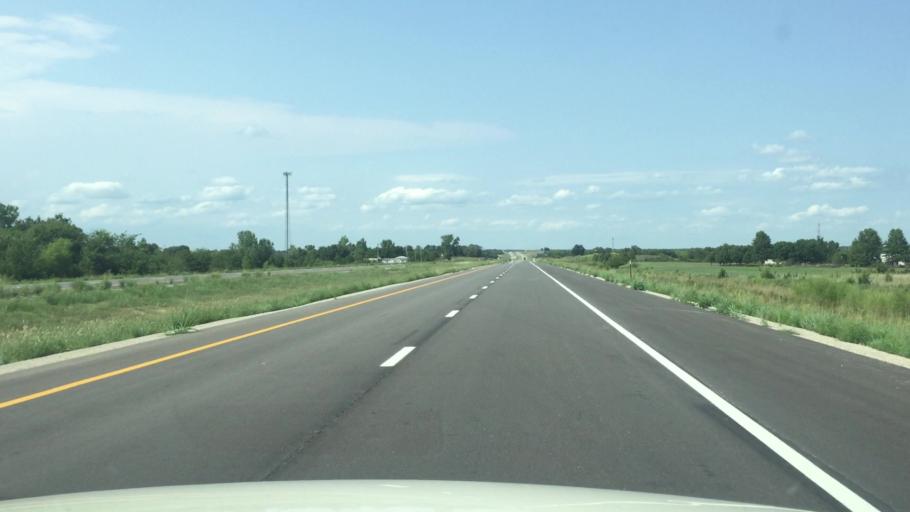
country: US
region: Kansas
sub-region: Linn County
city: La Cygne
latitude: 38.3701
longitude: -94.6873
